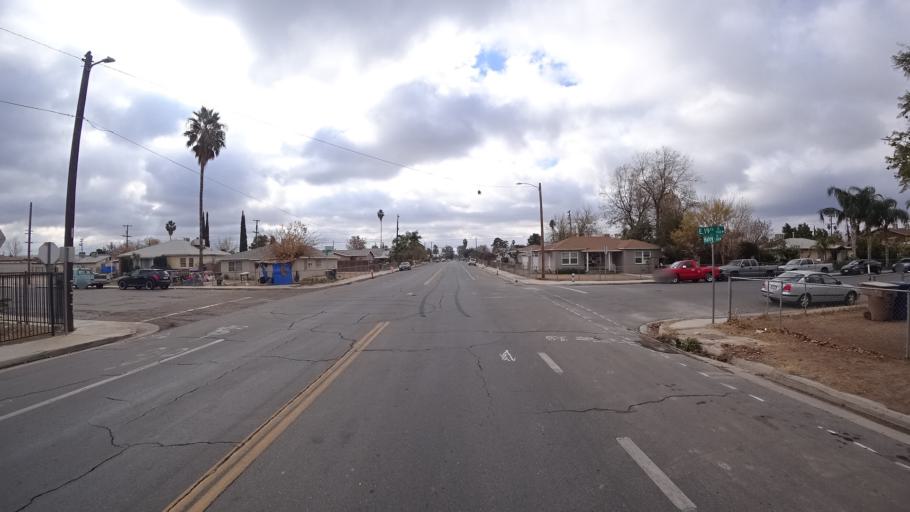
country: US
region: California
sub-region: Kern County
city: Bakersfield
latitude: 35.3724
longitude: -118.9828
